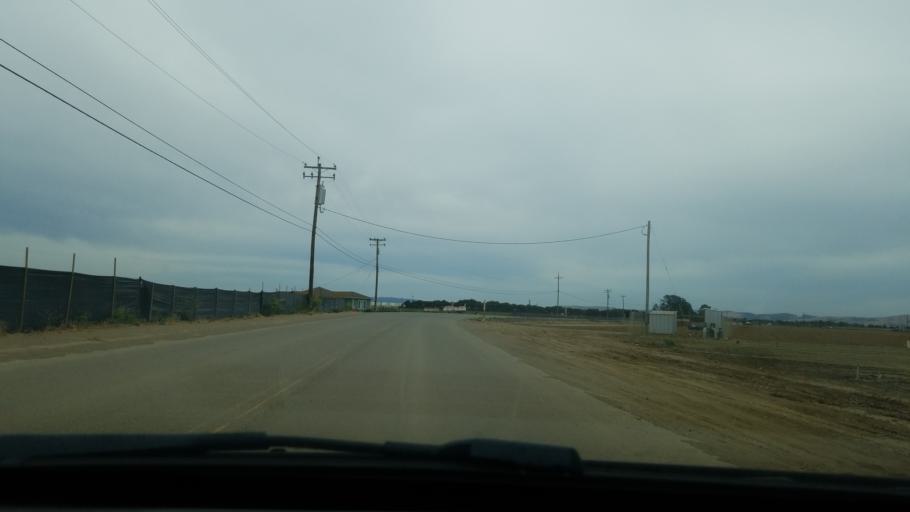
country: US
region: California
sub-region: San Luis Obispo County
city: Nipomo
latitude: 34.9964
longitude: -120.5146
